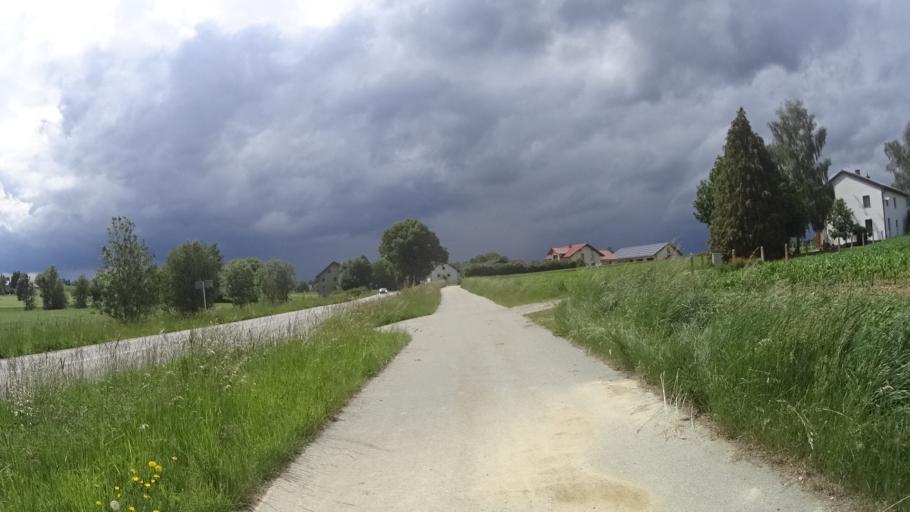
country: DE
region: Bavaria
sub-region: Upper Bavaria
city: Egglkofen
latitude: 48.4479
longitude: 12.4941
